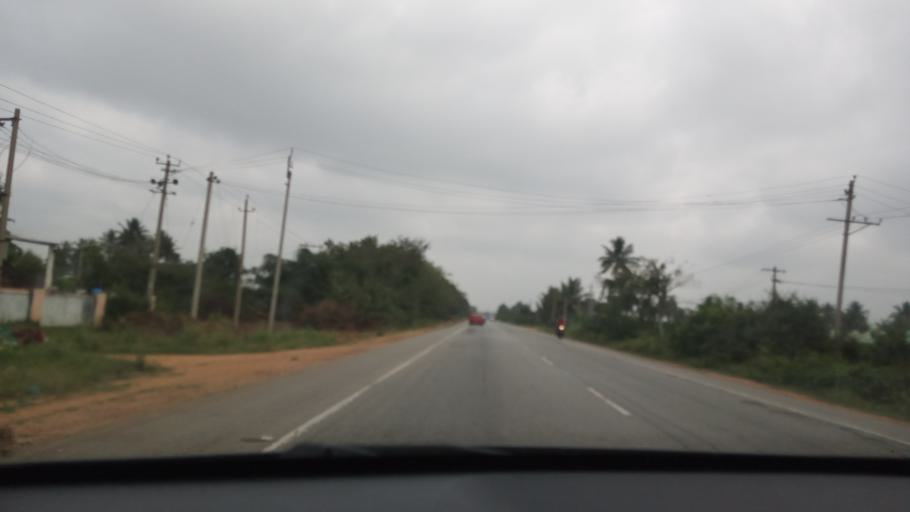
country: IN
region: Karnataka
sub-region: Chikkaballapur
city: Chintamani
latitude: 13.3423
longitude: 78.0127
